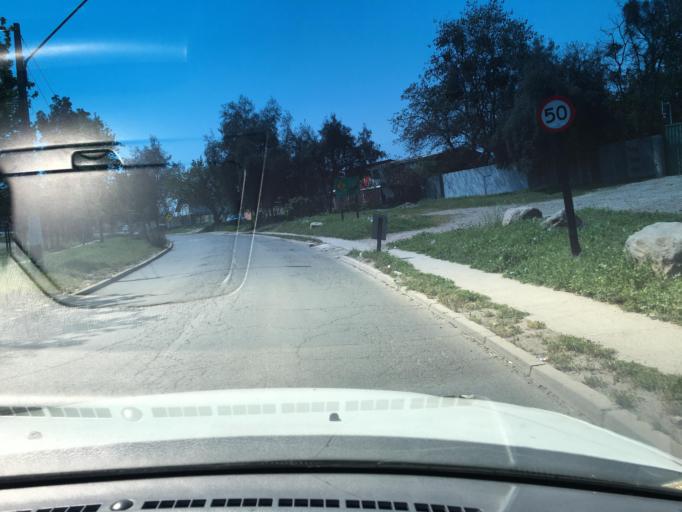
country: CL
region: Santiago Metropolitan
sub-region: Provincia de Santiago
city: Villa Presidente Frei, Nunoa, Santiago, Chile
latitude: -33.5160
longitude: -70.5504
